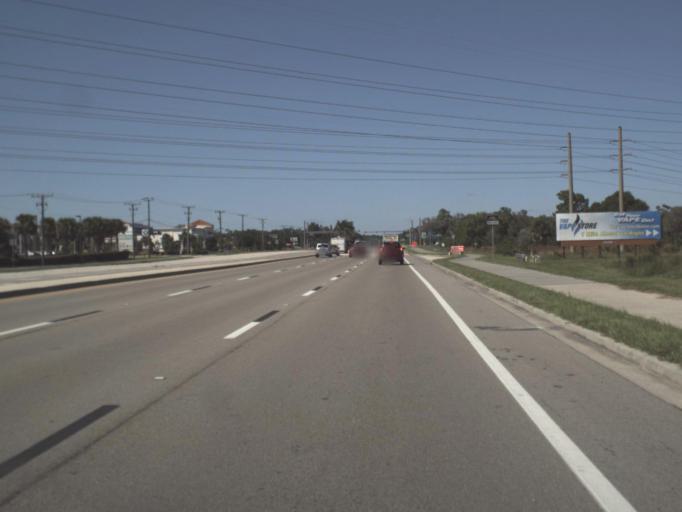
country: US
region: Florida
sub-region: Lee County
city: San Carlos Park
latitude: 26.4925
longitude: -81.8460
